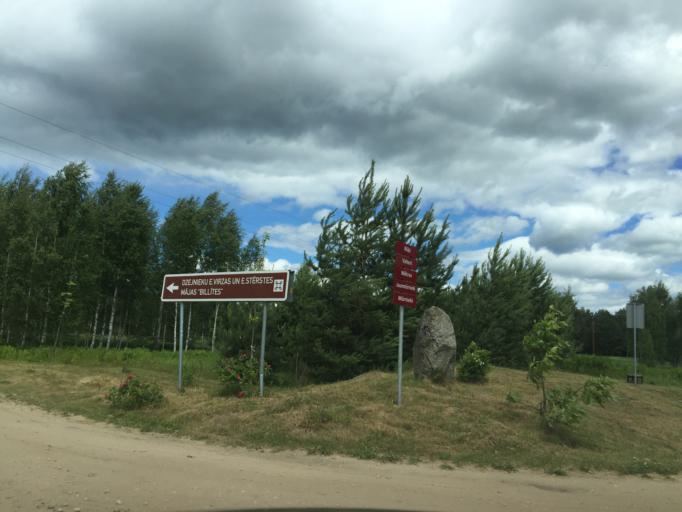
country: LV
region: Lecava
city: Iecava
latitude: 56.5728
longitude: 24.1145
